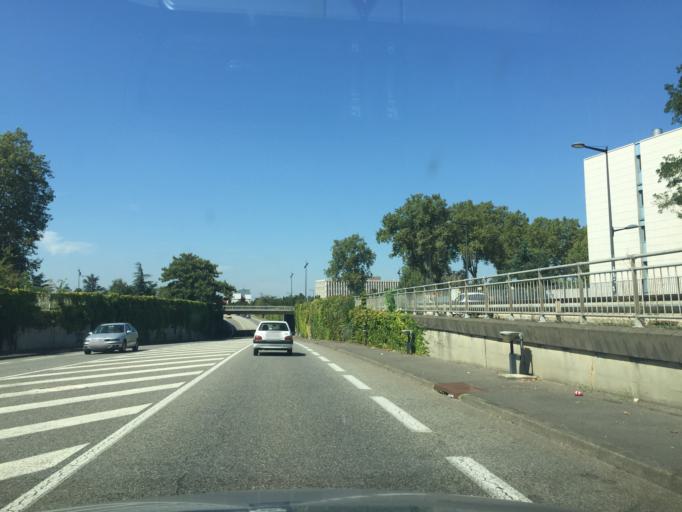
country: FR
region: Midi-Pyrenees
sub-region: Departement de la Haute-Garonne
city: Ramonville-Saint-Agne
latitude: 43.5623
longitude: 1.4620
